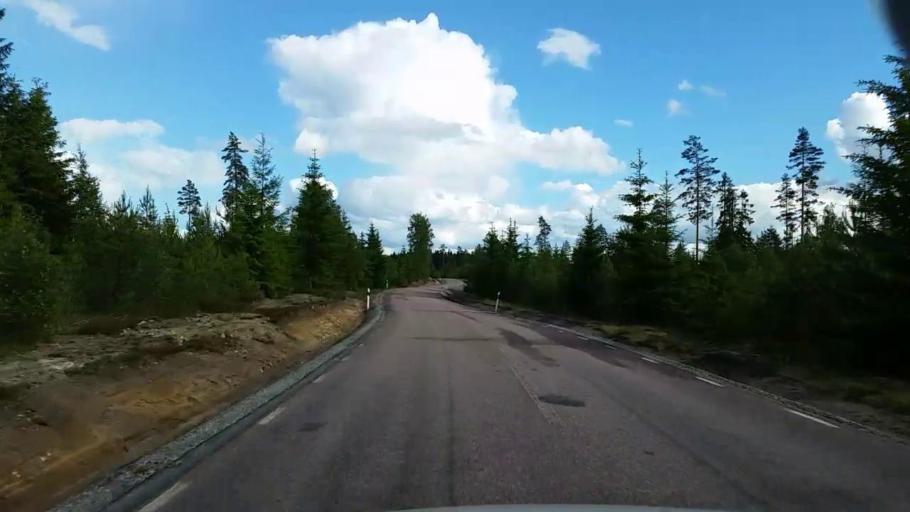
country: SE
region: Vaestmanland
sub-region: Fagersta Kommun
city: Fagersta
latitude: 59.8911
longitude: 15.8243
